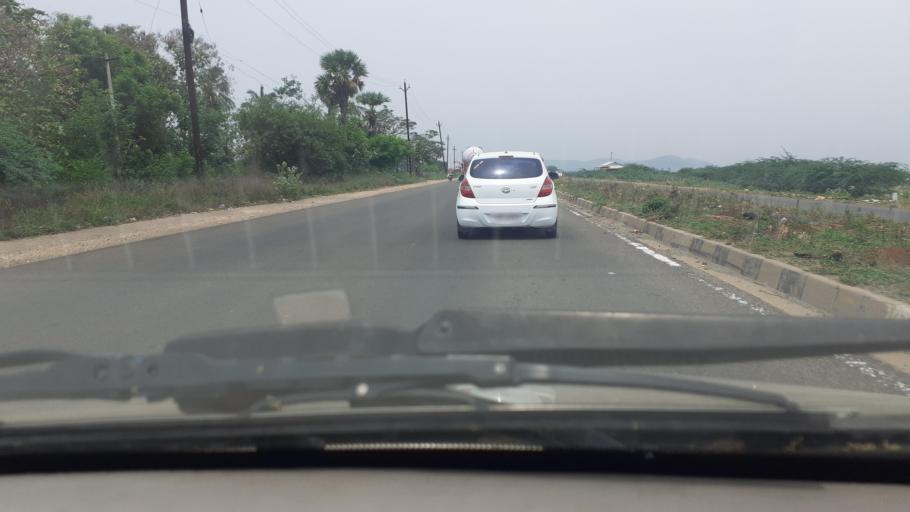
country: IN
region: Tamil Nadu
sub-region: Tirunelveli Kattabo
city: Tirunelveli
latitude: 8.7130
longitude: 77.7959
